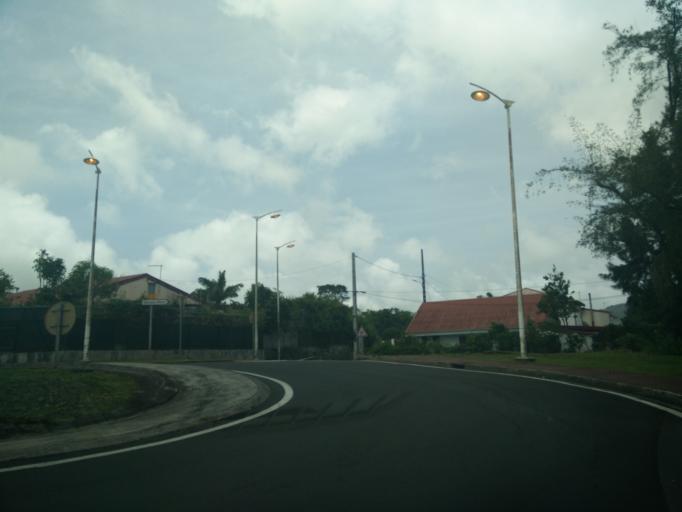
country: MQ
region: Martinique
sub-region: Martinique
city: Le Morne-Rouge
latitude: 14.7802
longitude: -61.1362
